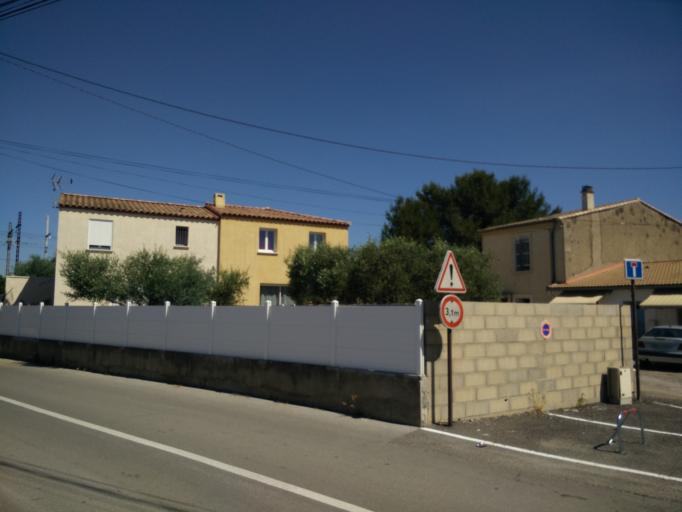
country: FR
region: Languedoc-Roussillon
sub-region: Departement du Gard
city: Uchaud
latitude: 43.7548
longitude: 4.2628
